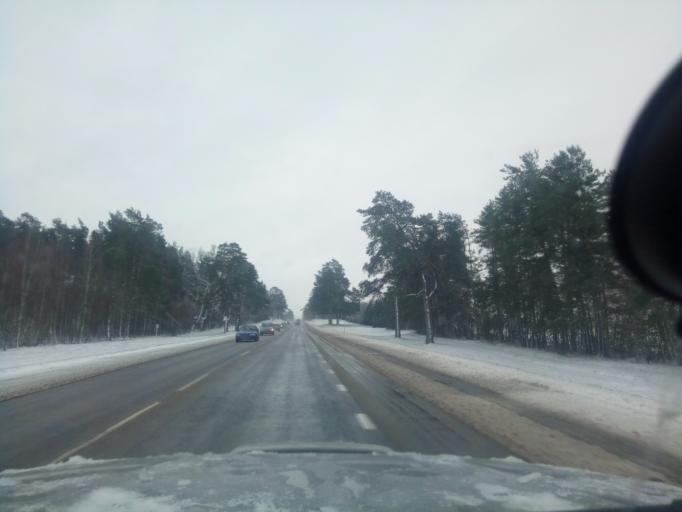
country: BY
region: Minsk
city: Nyasvizh
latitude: 53.2551
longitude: 26.6163
